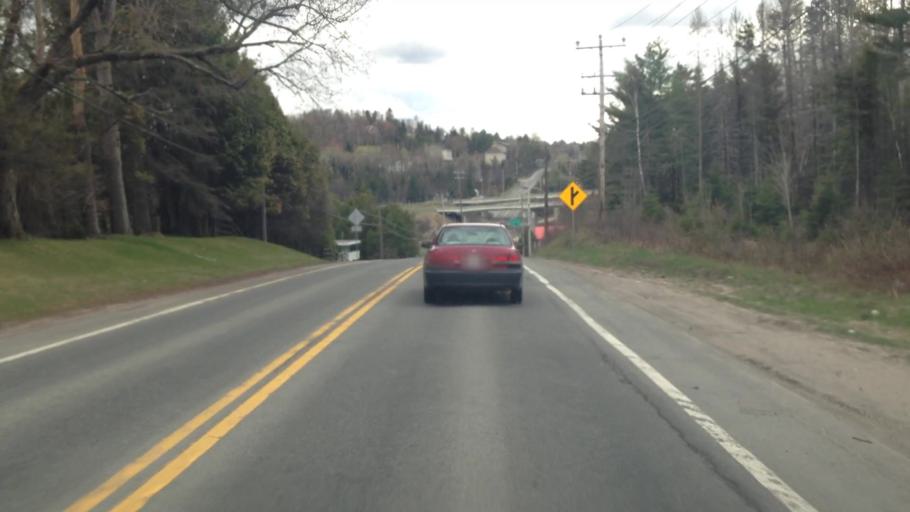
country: CA
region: Quebec
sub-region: Laurentides
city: Sainte-Adele
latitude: 45.9596
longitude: -74.1266
